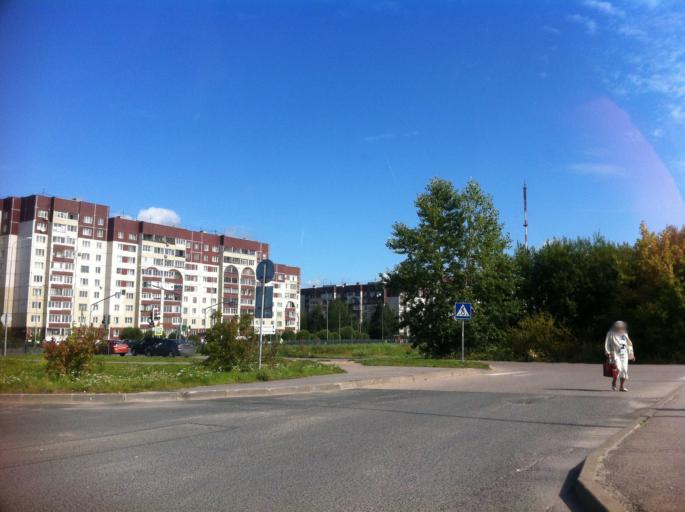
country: RU
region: Pskov
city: Pskov
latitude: 57.8066
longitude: 28.2683
